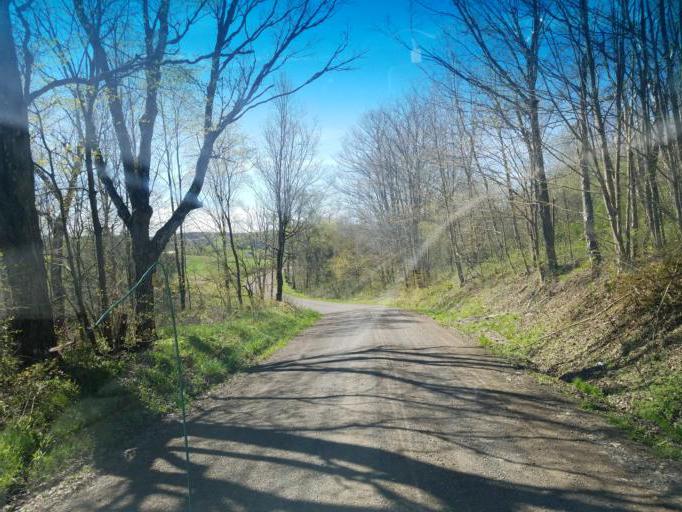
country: US
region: New York
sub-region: Allegany County
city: Andover
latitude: 41.9587
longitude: -77.7804
